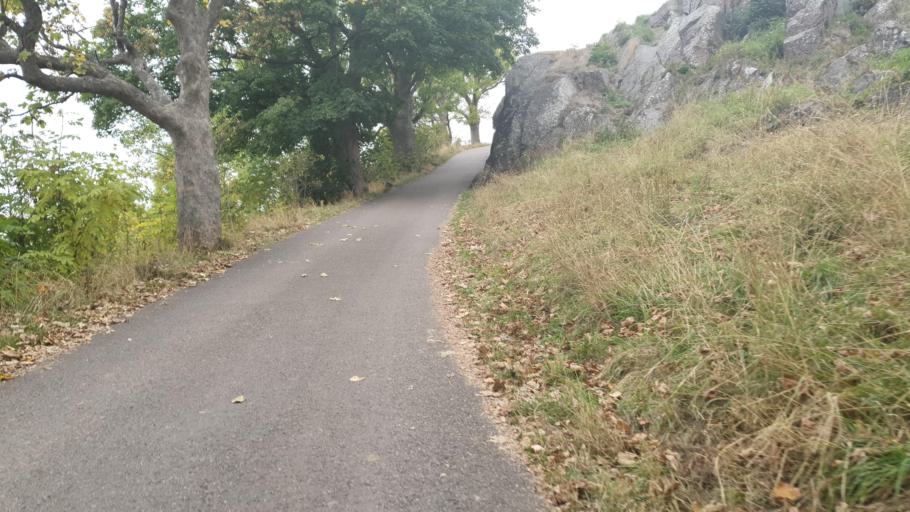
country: NO
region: Vestfold
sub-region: Tonsberg
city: Tonsberg
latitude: 59.2703
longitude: 10.4047
